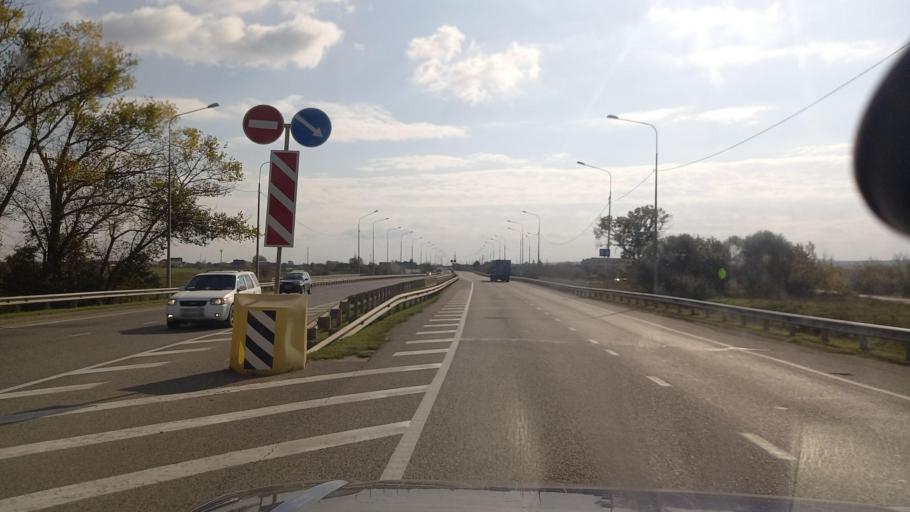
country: RU
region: Krasnodarskiy
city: Novoukrainskiy
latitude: 44.9011
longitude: 38.0371
